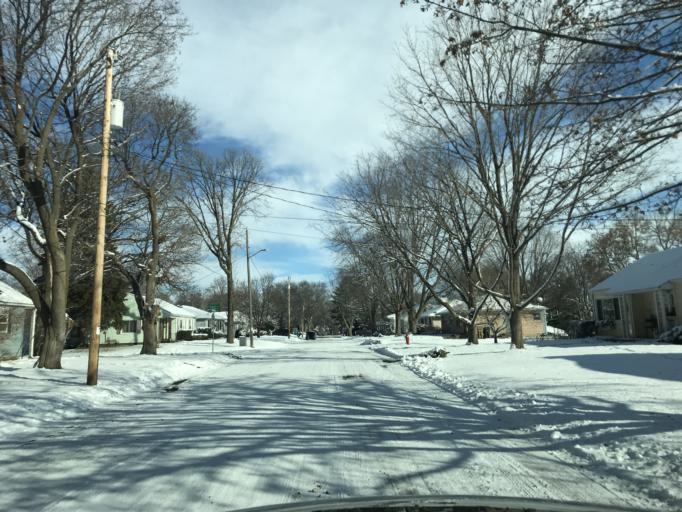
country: US
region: Wisconsin
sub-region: Dane County
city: Monona
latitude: 43.0762
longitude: -89.3144
